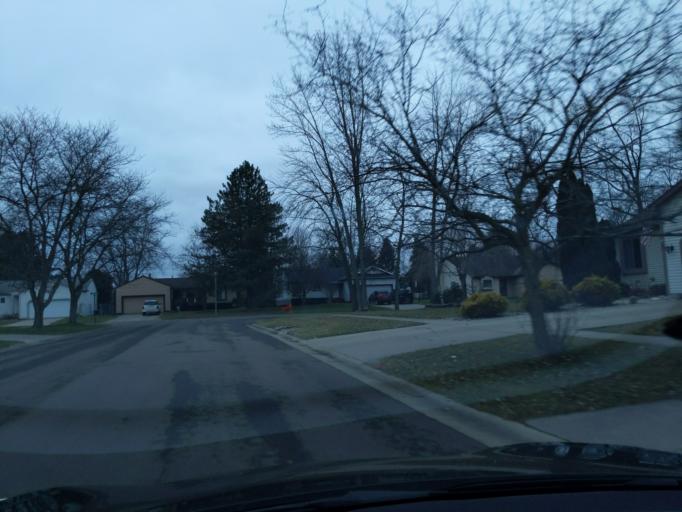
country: US
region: Michigan
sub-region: Eaton County
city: Waverly
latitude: 42.7366
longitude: -84.6121
